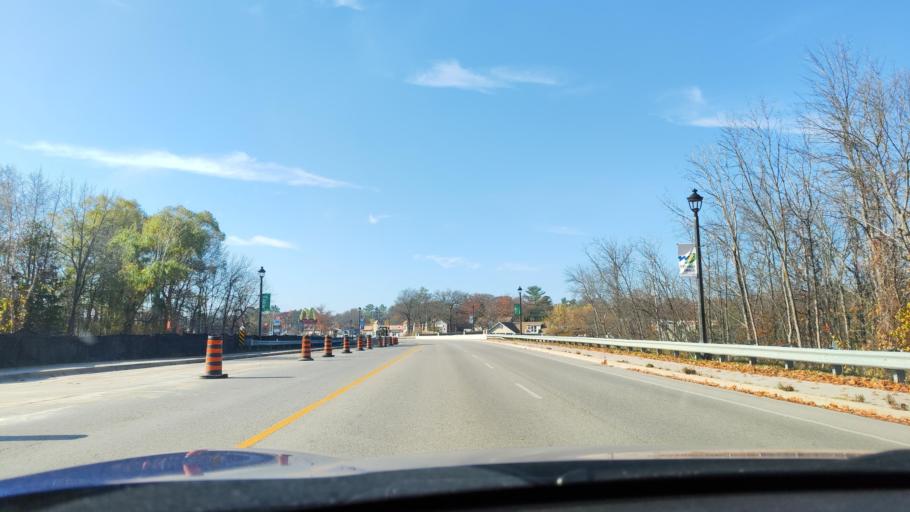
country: CA
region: Ontario
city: Wasaga Beach
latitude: 44.4899
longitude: -80.0499
